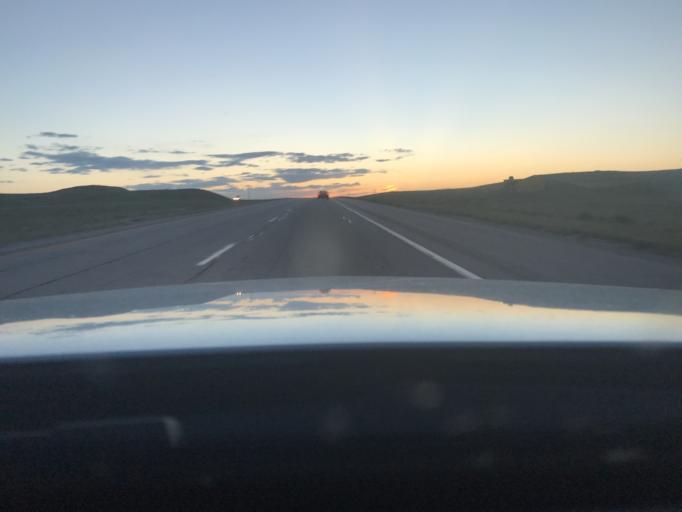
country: US
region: Wyoming
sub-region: Converse County
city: Glenrock
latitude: 42.8341
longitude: -105.8471
